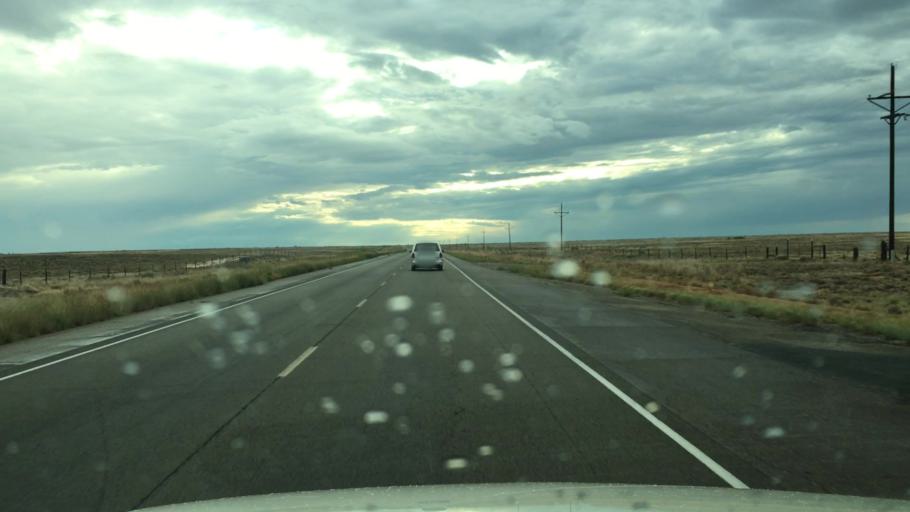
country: US
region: New Mexico
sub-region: Chaves County
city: Roswell
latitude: 33.4051
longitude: -104.3111
